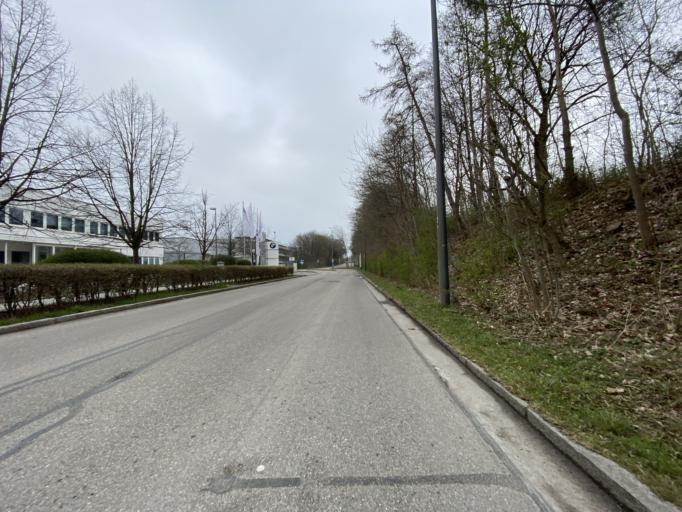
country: DE
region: Bavaria
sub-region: Upper Bavaria
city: Bogenhausen
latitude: 48.1908
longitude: 11.5811
